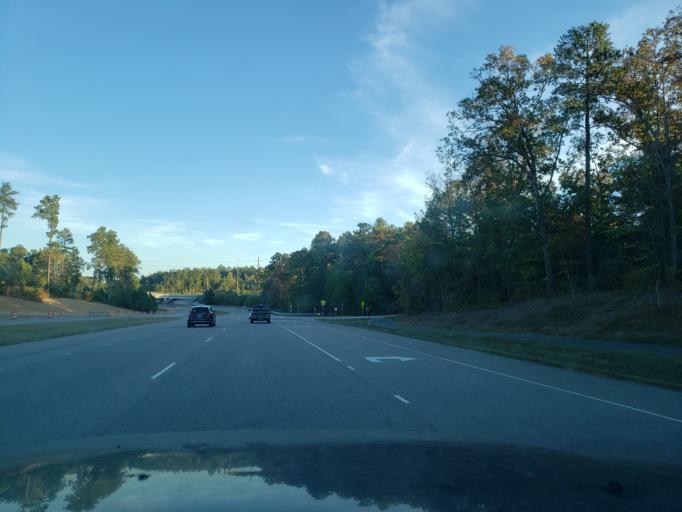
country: US
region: North Carolina
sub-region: Wake County
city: Morrisville
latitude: 35.8547
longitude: -78.8663
